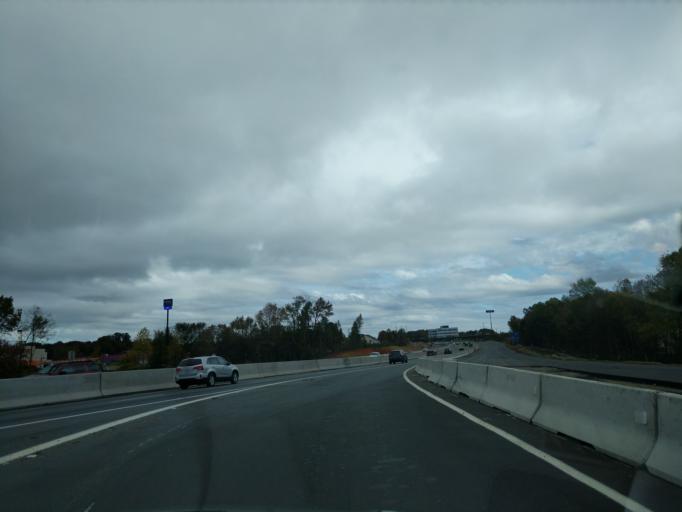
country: US
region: North Carolina
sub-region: Cabarrus County
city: Kannapolis
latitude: 35.4463
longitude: -80.6068
